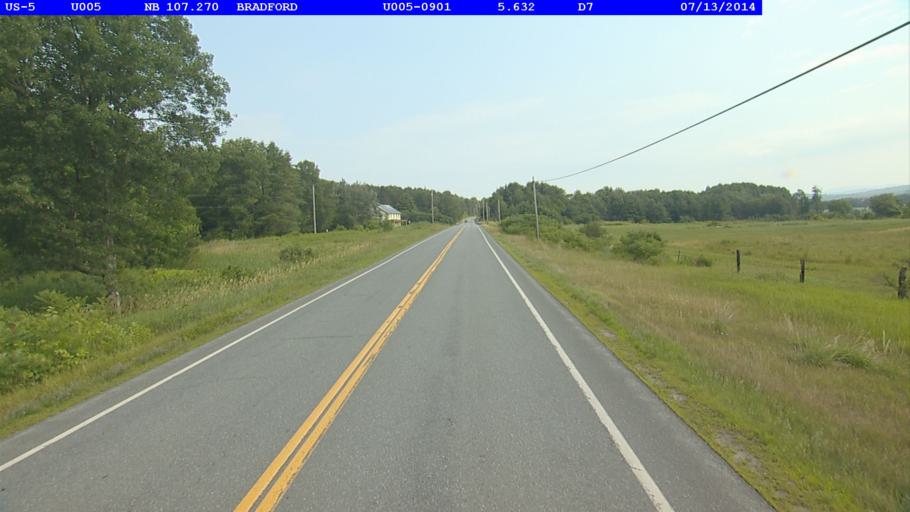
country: US
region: New Hampshire
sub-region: Grafton County
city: Haverhill
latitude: 44.0299
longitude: -72.0914
